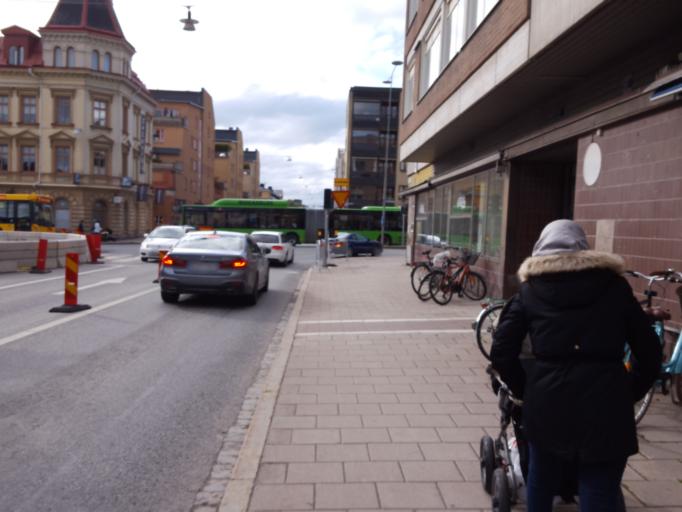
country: SE
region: Uppsala
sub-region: Uppsala Kommun
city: Uppsala
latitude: 59.8621
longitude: 17.6479
